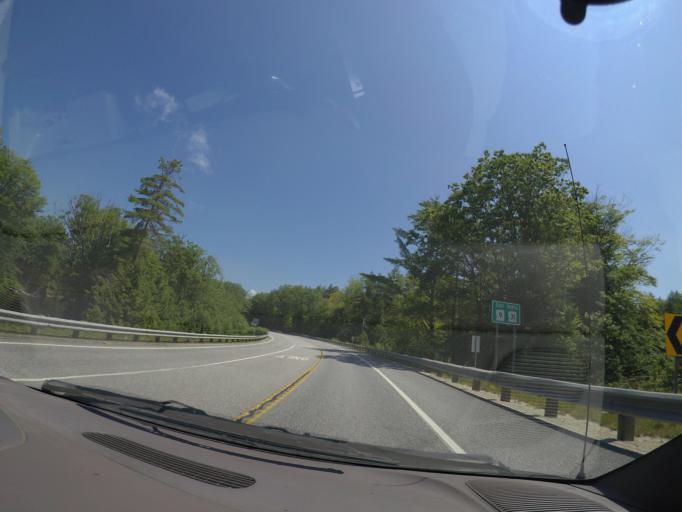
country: US
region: New Hampshire
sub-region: Hillsborough County
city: Antrim
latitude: 43.0755
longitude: -71.9808
